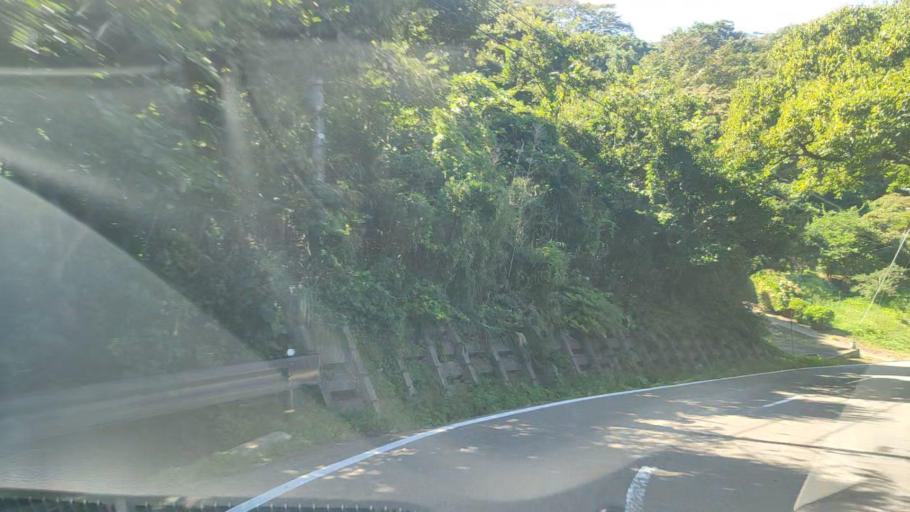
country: JP
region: Ishikawa
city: Nanao
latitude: 37.5272
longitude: 137.2656
